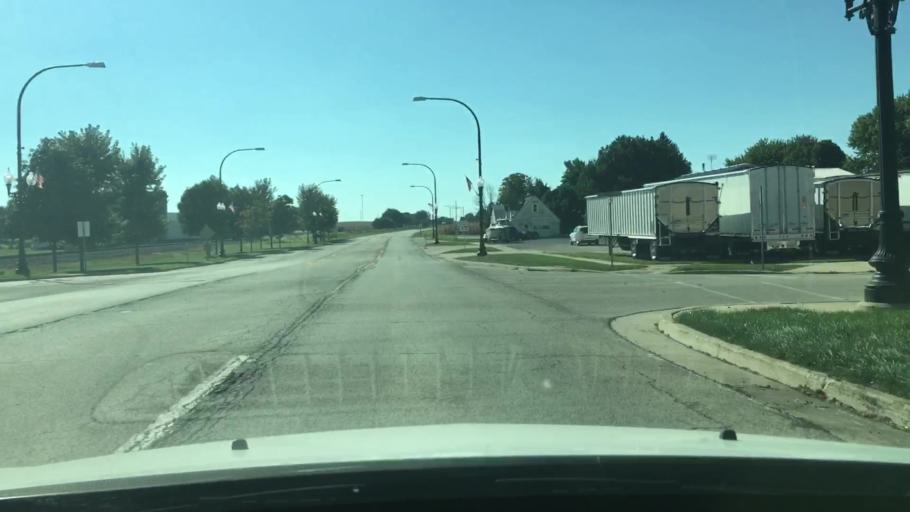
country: US
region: Illinois
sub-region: DeKalb County
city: Waterman
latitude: 41.7690
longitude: -88.7765
